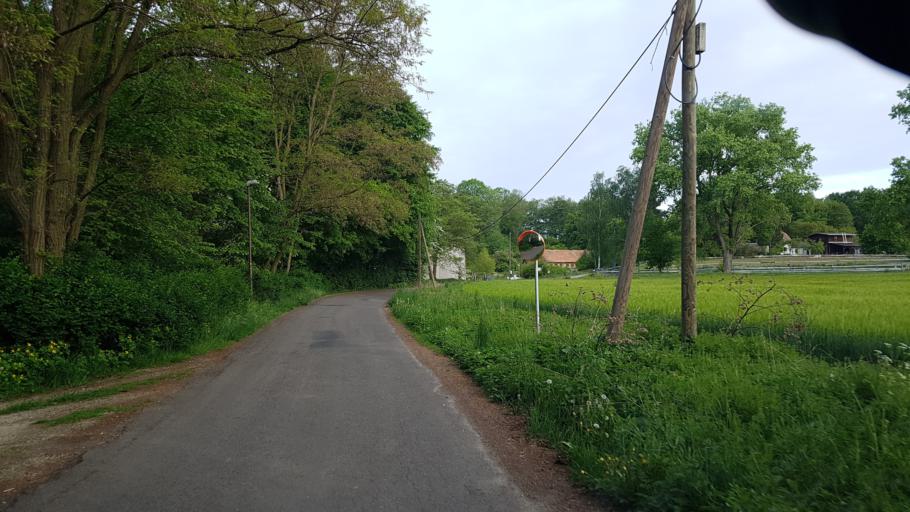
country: DE
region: Brandenburg
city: Luckau
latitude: 51.8090
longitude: 13.6334
